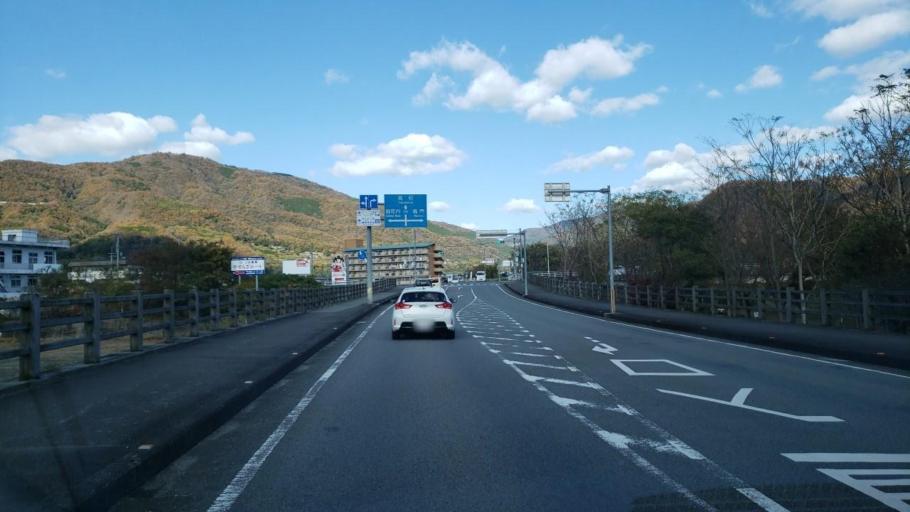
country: JP
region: Tokushima
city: Wakimachi
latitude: 34.0771
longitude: 134.1729
